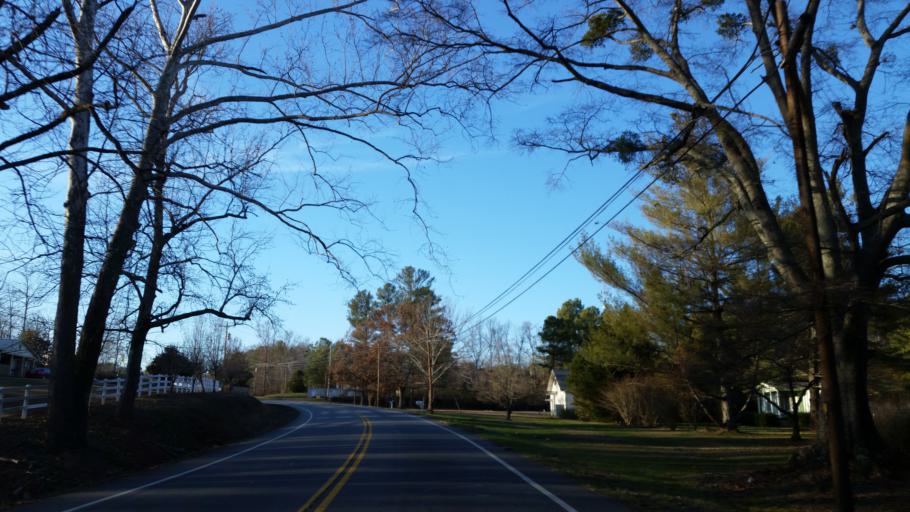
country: US
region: Georgia
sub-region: Gordon County
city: Calhoun
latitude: 34.6302
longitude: -84.9564
